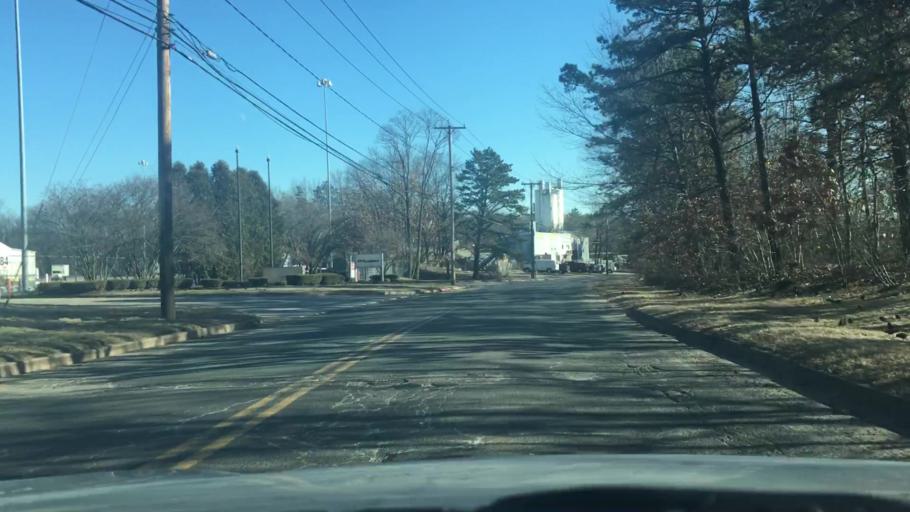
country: US
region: Massachusetts
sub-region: Hampden County
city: North Chicopee
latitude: 42.1669
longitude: -72.5403
